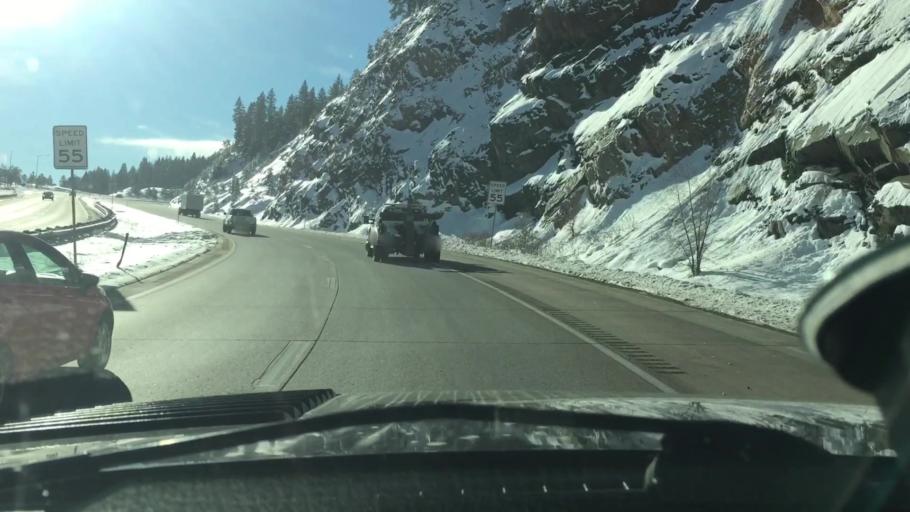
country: US
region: Colorado
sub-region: Jefferson County
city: Indian Hills
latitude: 39.6089
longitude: -105.2319
